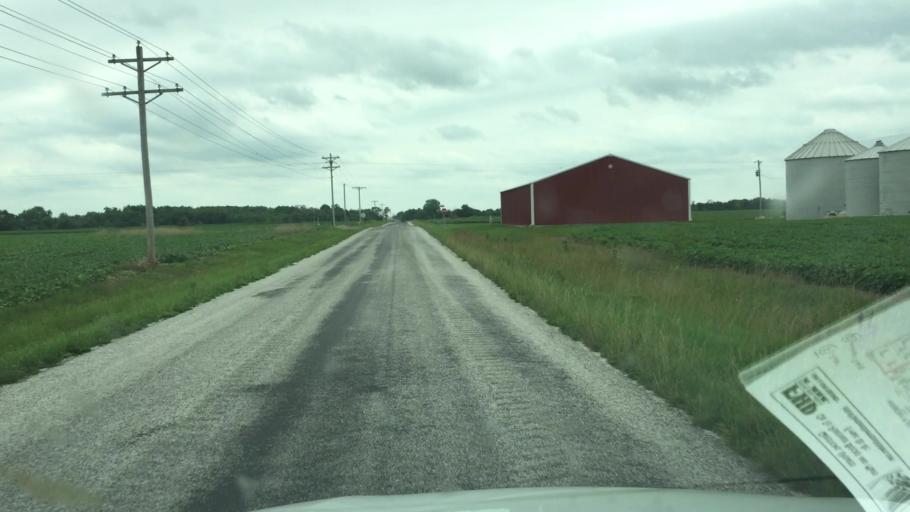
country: US
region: Illinois
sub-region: Hancock County
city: Carthage
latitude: 40.2914
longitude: -91.0833
